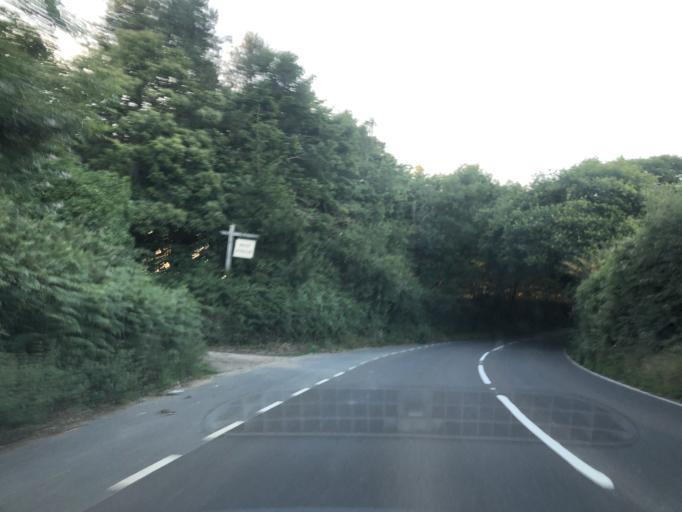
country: GB
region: England
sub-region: Isle of Wight
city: Newport
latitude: 50.6675
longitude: -1.2849
